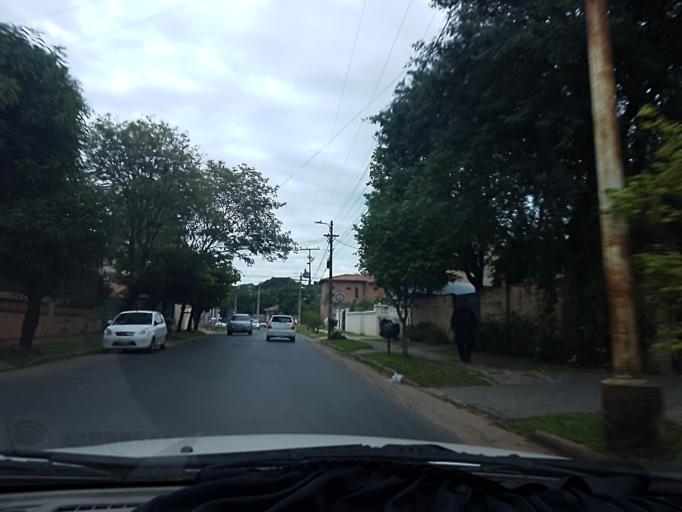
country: PY
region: Asuncion
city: Asuncion
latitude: -25.2620
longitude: -57.5784
